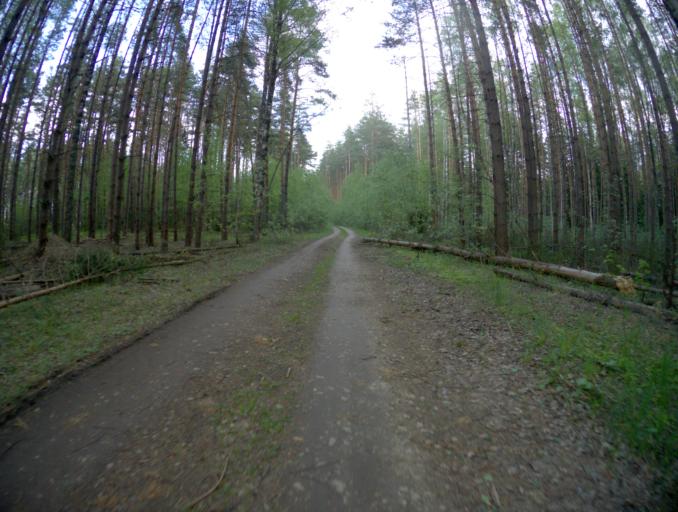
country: RU
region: Rjazan
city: Spas-Klepiki
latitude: 55.2399
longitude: 40.0609
